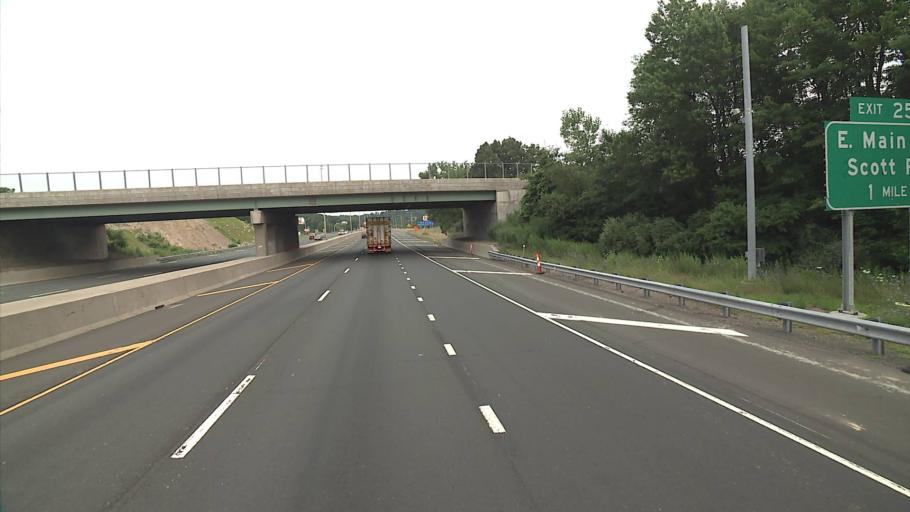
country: US
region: Connecticut
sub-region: New Haven County
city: Prospect
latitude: 41.5404
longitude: -72.9746
